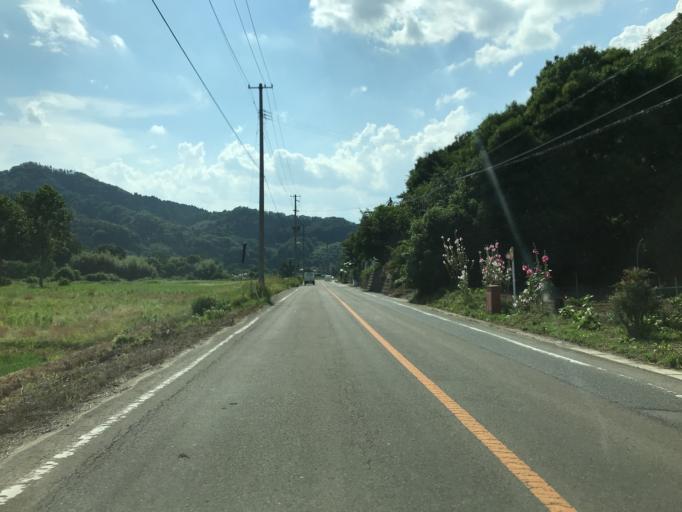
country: JP
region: Fukushima
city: Yanagawamachi-saiwaicho
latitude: 37.8055
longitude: 140.6249
